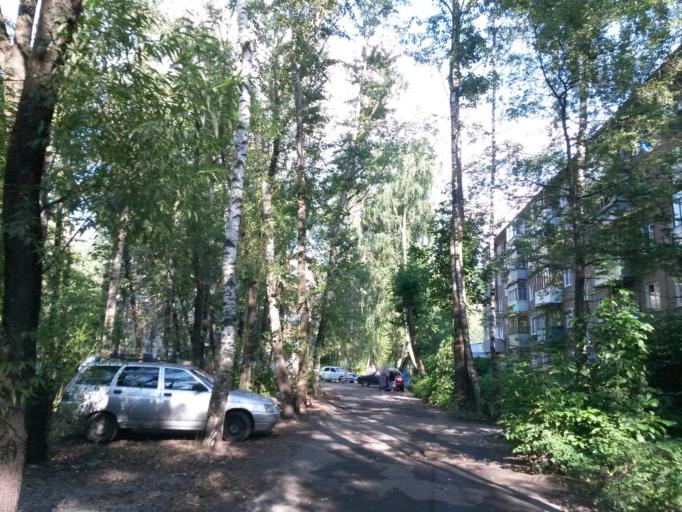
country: RU
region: Ivanovo
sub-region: Gorod Ivanovo
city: Ivanovo
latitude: 56.9581
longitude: 40.9888
